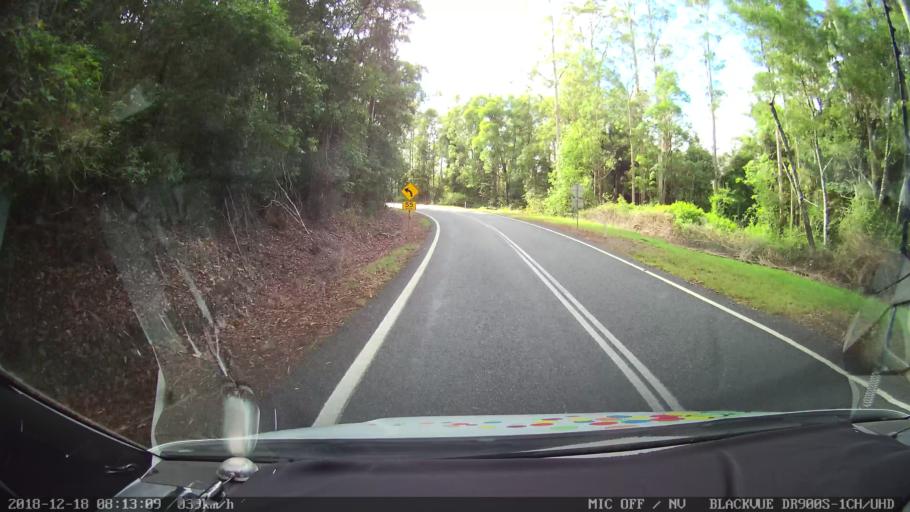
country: AU
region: New South Wales
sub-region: Kyogle
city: Kyogle
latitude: -28.3368
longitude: 152.6741
